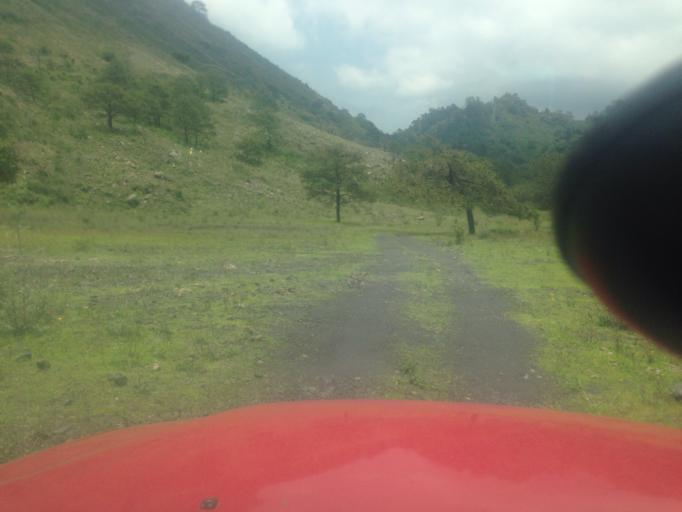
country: MX
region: Nayarit
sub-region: Ahuacatlan
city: Ahuacatlan
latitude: 21.1155
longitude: -104.5028
